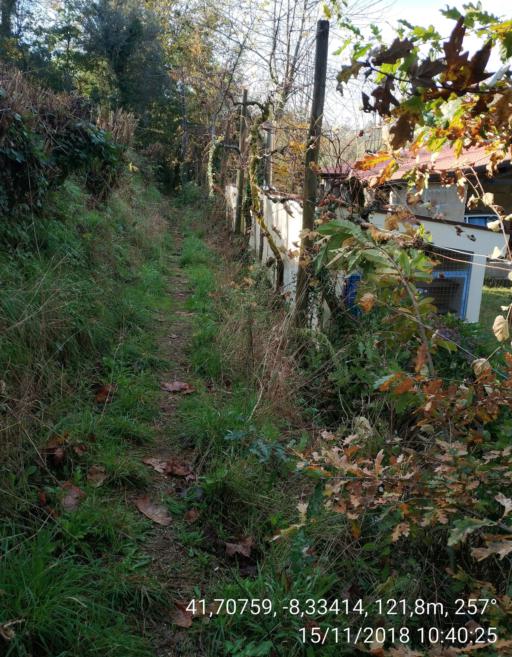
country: PT
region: Braga
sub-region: Terras de Bouro
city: Terras de Bouro
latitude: 41.7077
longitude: -8.3341
